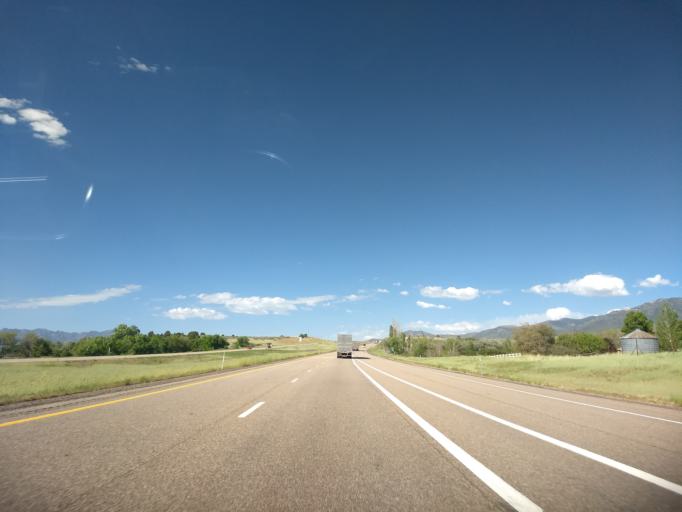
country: US
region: Utah
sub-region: Millard County
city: Fillmore
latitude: 39.0872
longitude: -112.2723
